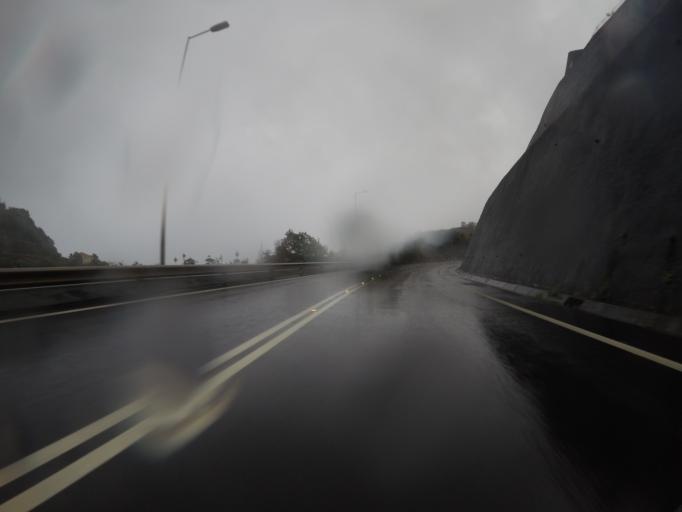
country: PT
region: Madeira
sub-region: Santana
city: Santana
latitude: 32.7634
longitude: -16.8327
